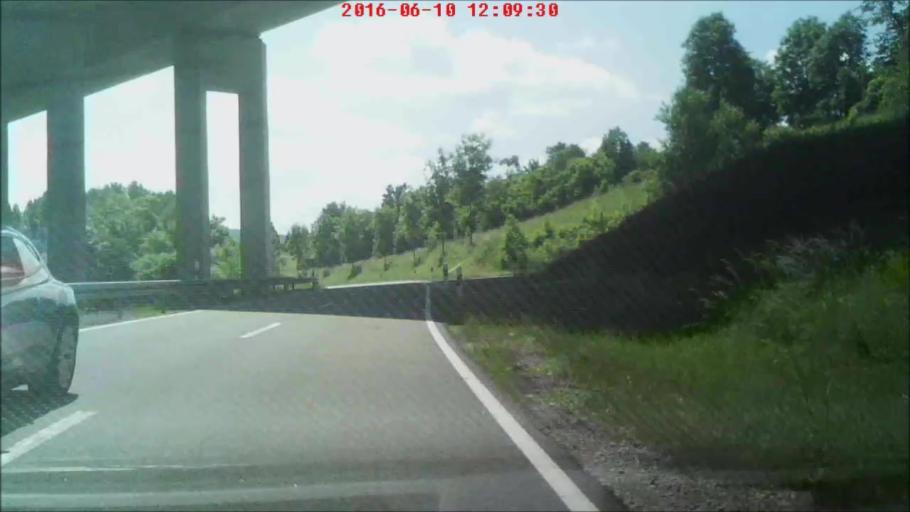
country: DE
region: Thuringia
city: Ellingshausen
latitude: 50.5531
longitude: 10.4745
